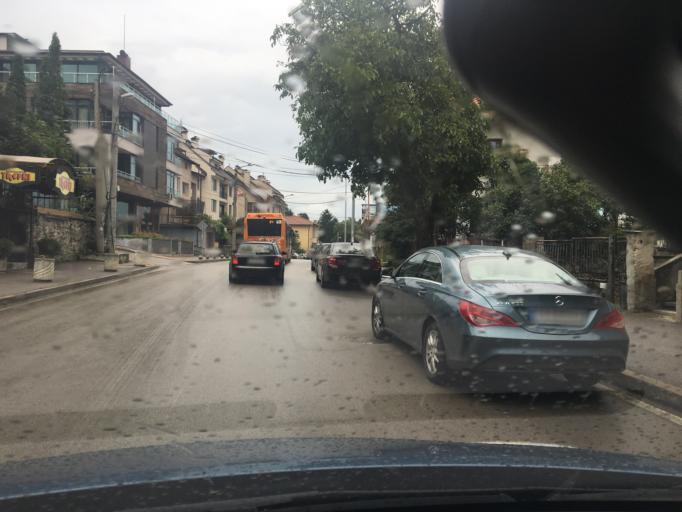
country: BG
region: Sofia-Capital
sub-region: Stolichna Obshtina
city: Sofia
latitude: 42.6293
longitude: 23.3086
